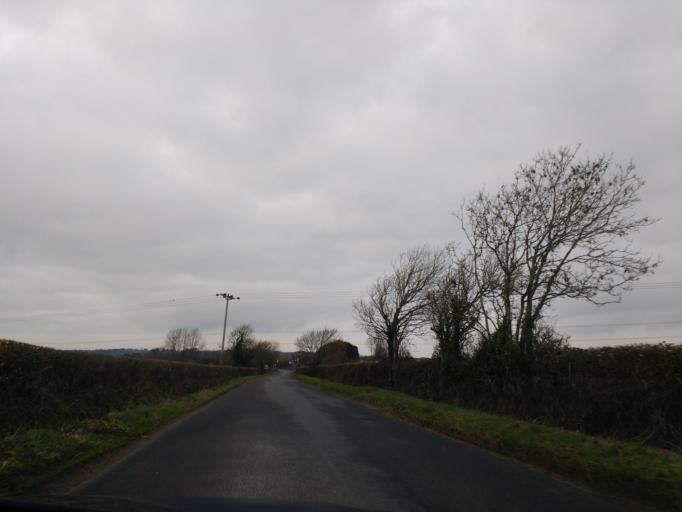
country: GB
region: England
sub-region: Isle of Wight
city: Shalfleet
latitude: 50.6973
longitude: -1.4060
